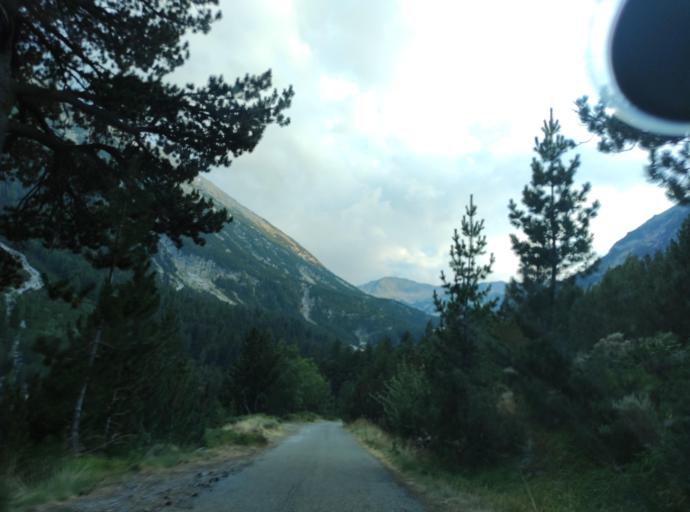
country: BG
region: Blagoevgrad
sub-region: Obshtina Bansko
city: Bansko
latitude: 41.7651
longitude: 23.4205
